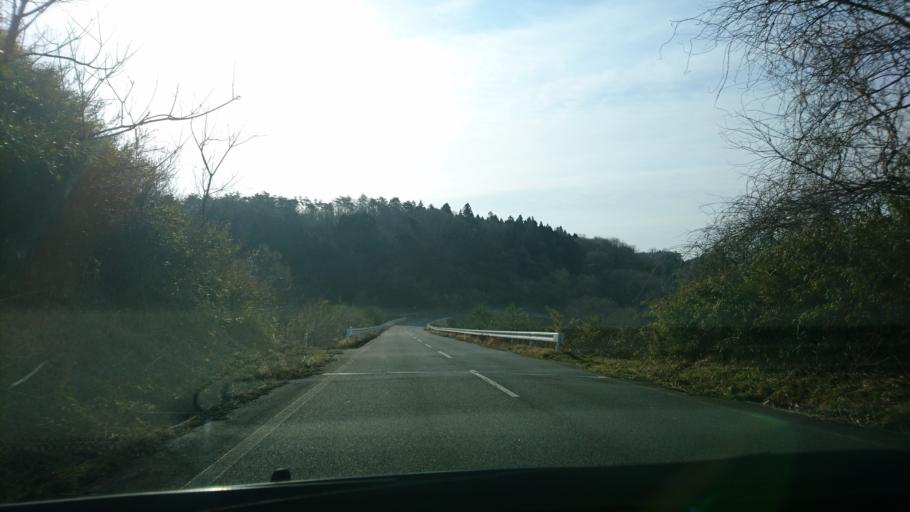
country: JP
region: Iwate
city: Ichinoseki
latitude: 38.8621
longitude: 141.1972
